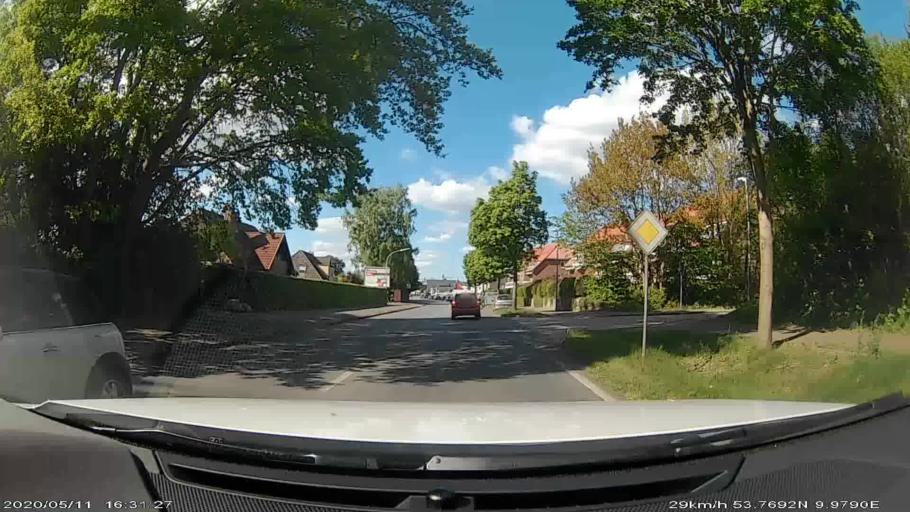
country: DE
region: Schleswig-Holstein
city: Henstedt-Ulzburg
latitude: 53.7711
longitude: 9.9875
